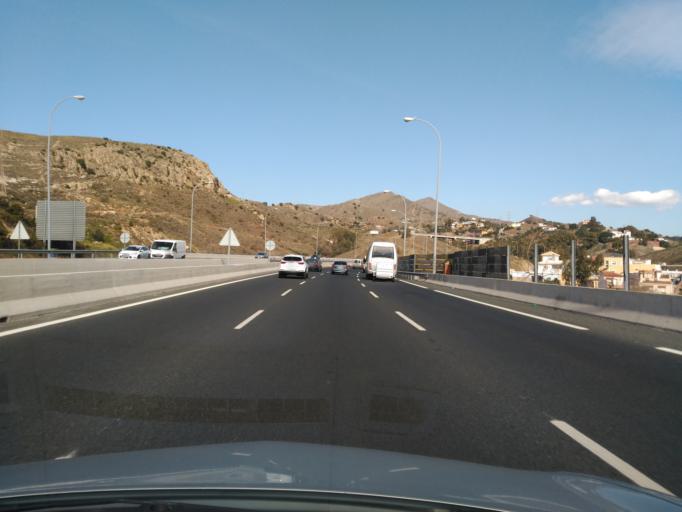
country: ES
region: Andalusia
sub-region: Provincia de Malaga
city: Malaga
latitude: 36.7355
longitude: -4.4540
